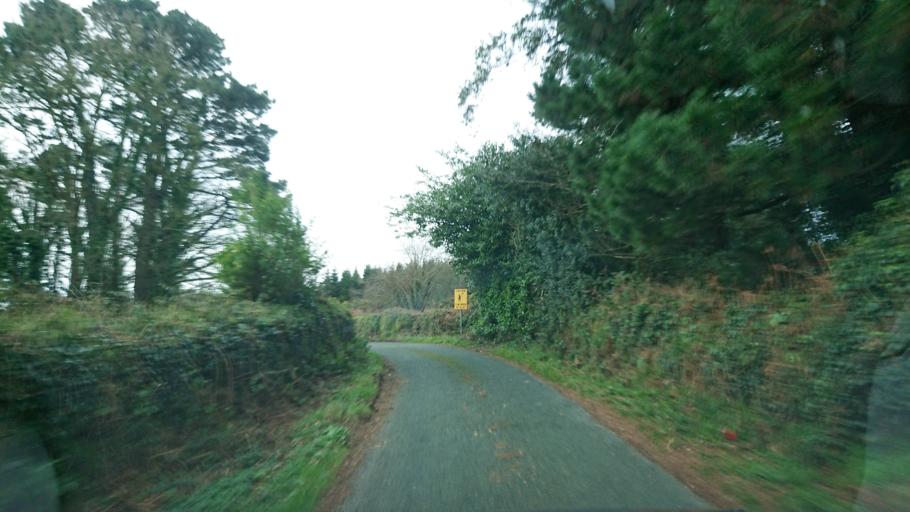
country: IE
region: Leinster
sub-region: Kilkenny
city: Mooncoin
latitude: 52.2156
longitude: -7.2716
